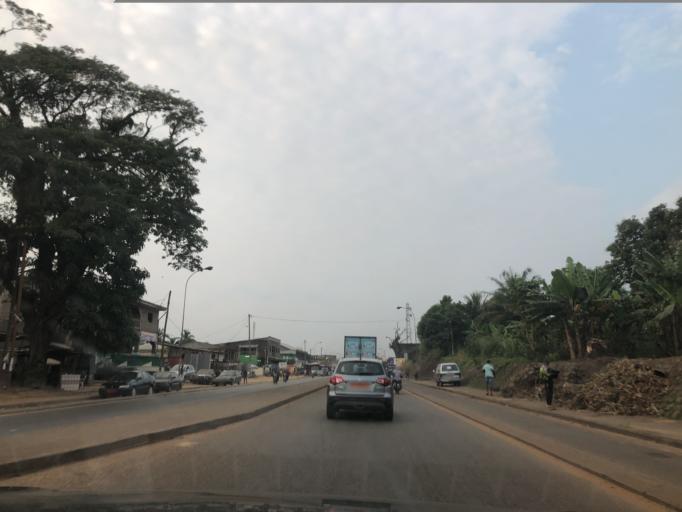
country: CM
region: Littoral
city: Edea
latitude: 3.7945
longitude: 10.1317
